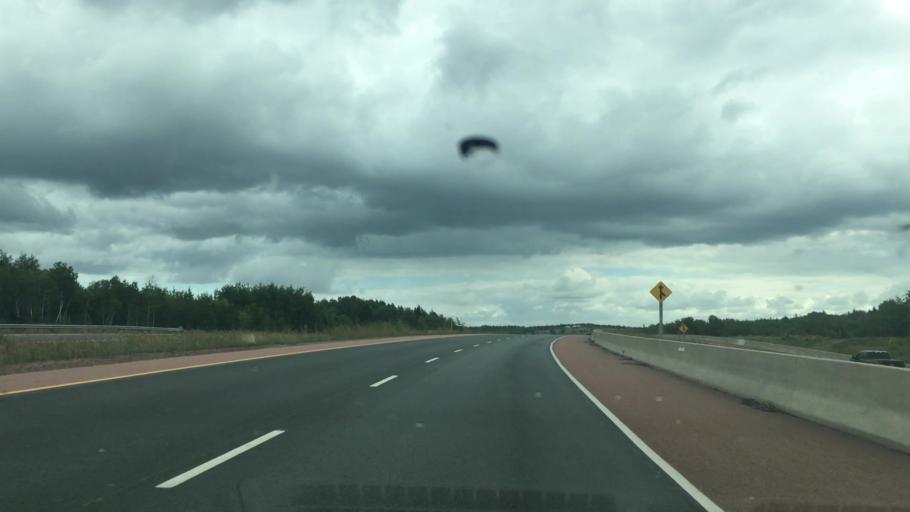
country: CA
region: Nova Scotia
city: Antigonish
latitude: 45.6111
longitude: -61.9973
